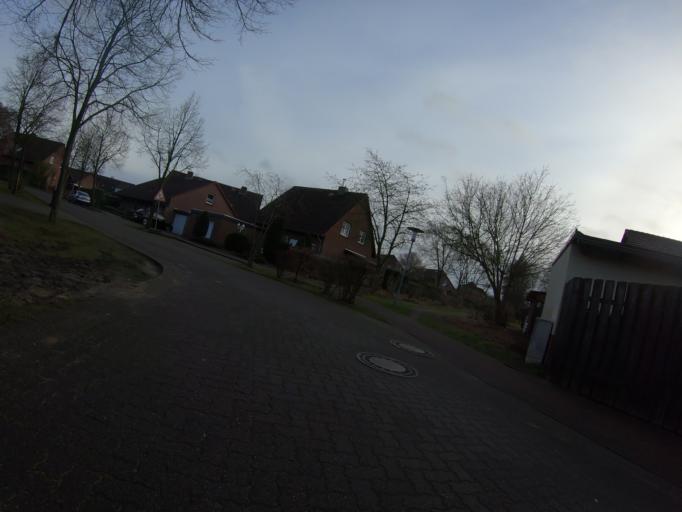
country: DE
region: Lower Saxony
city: Wesendorf
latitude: 52.5987
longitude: 10.5416
